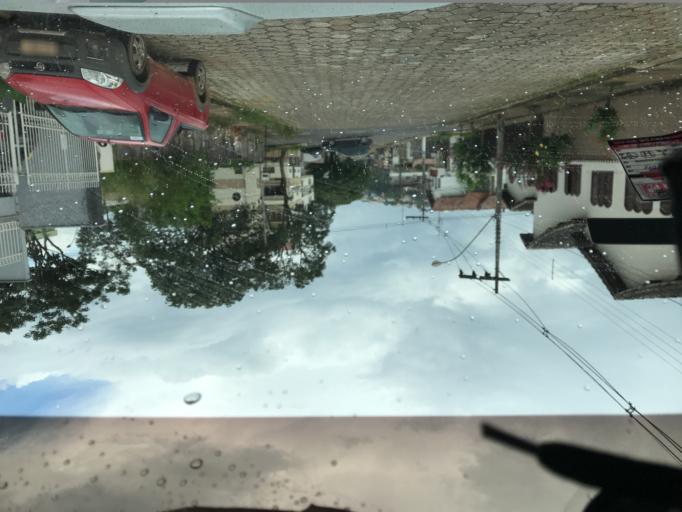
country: BR
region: Minas Gerais
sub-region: Tres Coracoes
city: Tres Coracoes
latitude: -21.7038
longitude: -45.2515
